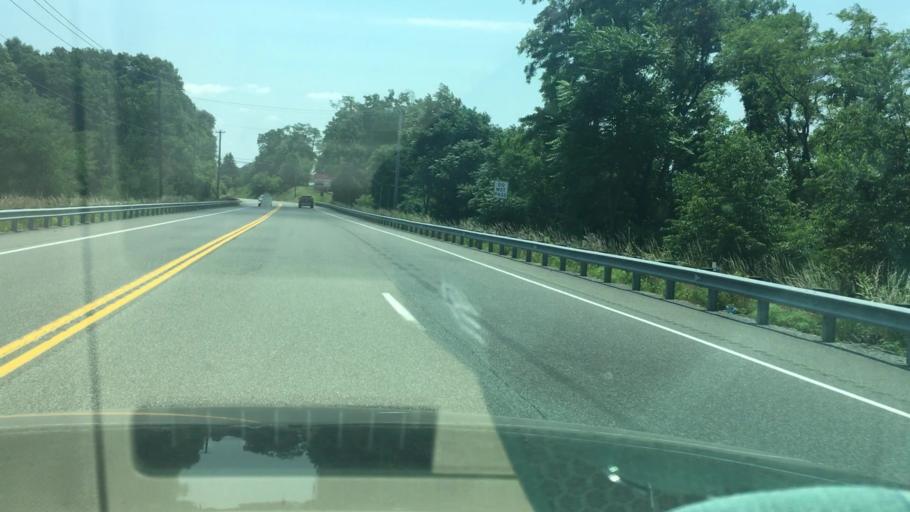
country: US
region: Pennsylvania
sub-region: Lehigh County
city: Schnecksville
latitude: 40.6177
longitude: -75.6591
